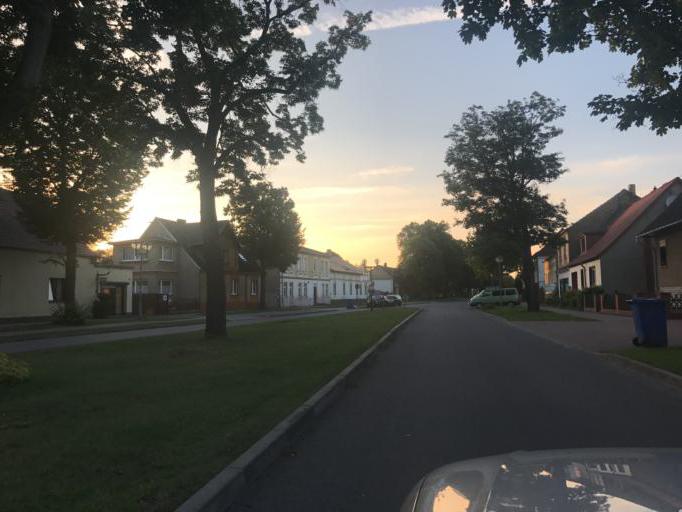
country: DE
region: Brandenburg
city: Melchow
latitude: 52.8504
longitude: 13.6829
